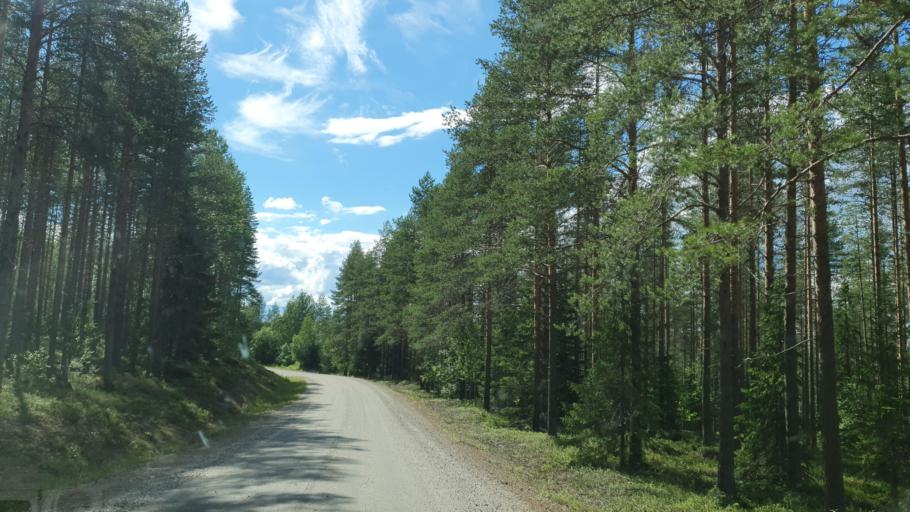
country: FI
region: Kainuu
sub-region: Kehys-Kainuu
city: Kuhmo
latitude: 64.1606
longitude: 29.8151
